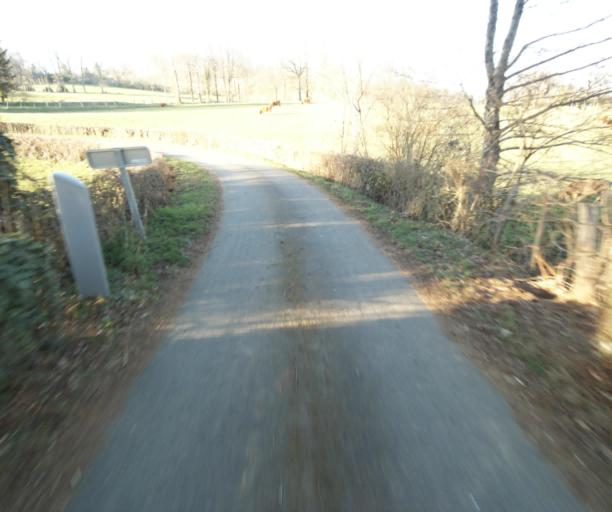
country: FR
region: Limousin
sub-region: Departement de la Correze
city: Saint-Clement
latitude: 45.3626
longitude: 1.6862
